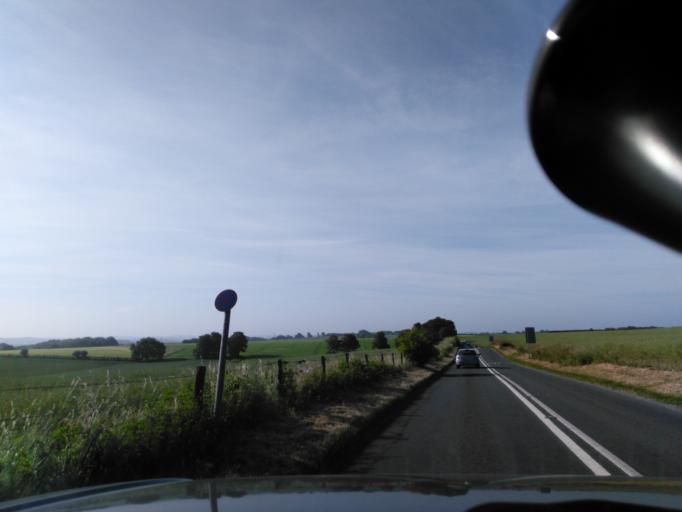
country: GB
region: England
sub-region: Wiltshire
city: Woodford
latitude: 51.1193
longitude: -1.8526
